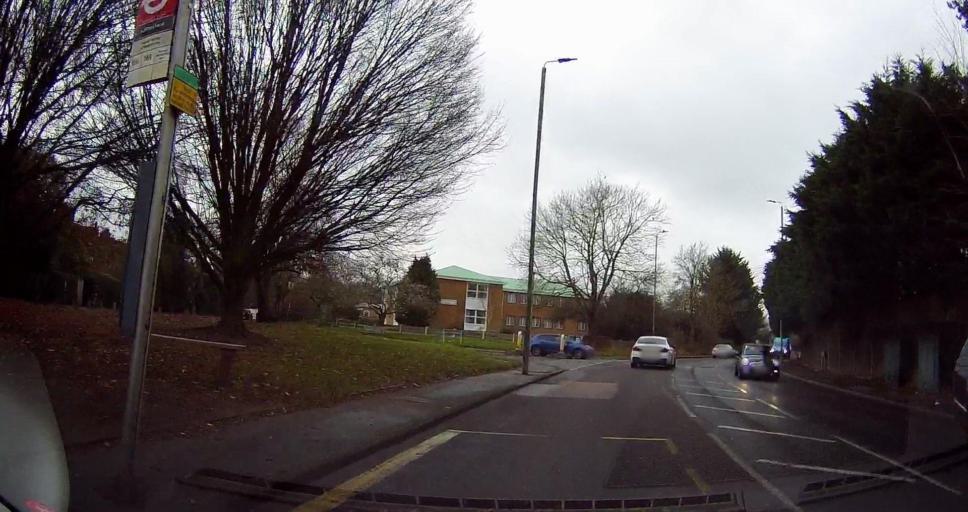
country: GB
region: England
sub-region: Greater London
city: Chislehurst
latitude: 51.4144
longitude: 0.0807
